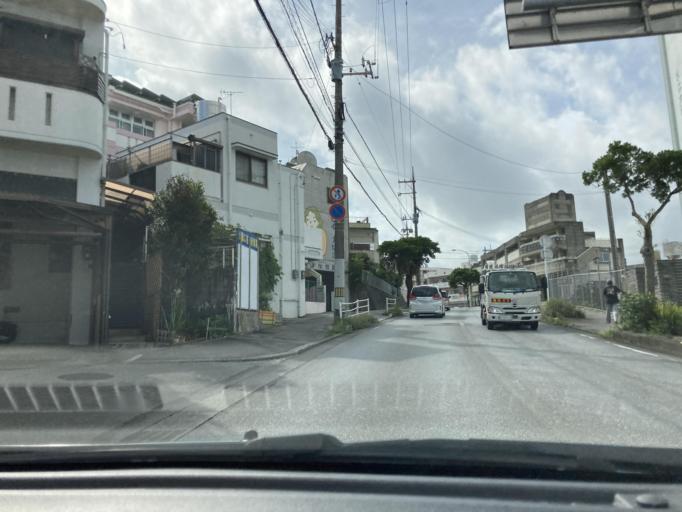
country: JP
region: Okinawa
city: Ginowan
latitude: 26.2609
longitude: 127.7637
